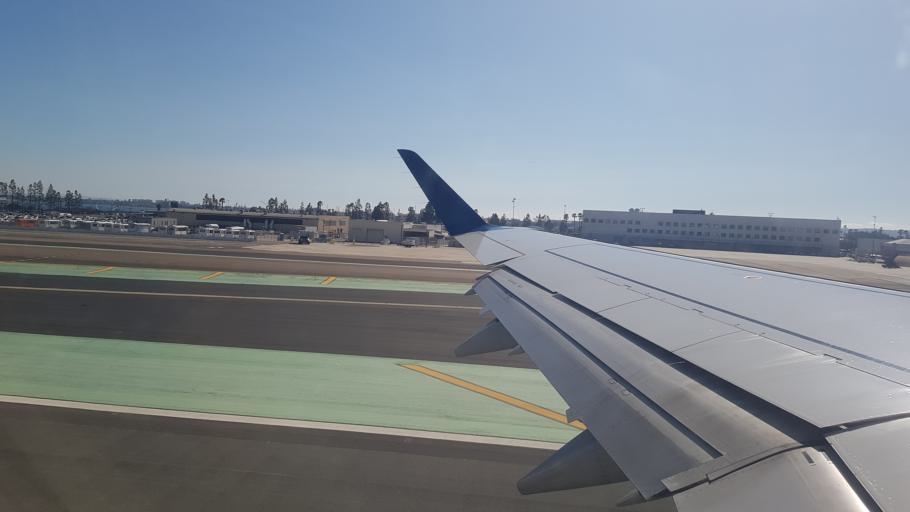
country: US
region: California
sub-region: San Diego County
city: San Diego
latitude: 32.7336
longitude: -117.1893
